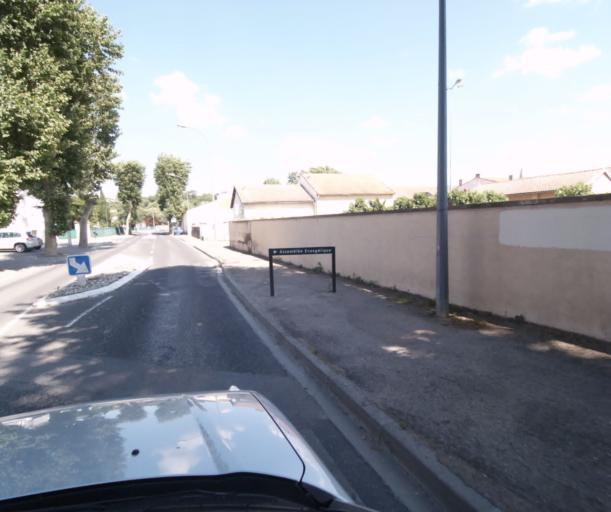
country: FR
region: Languedoc-Roussillon
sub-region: Departement de l'Aude
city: Limoux
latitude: 43.0570
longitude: 2.2192
